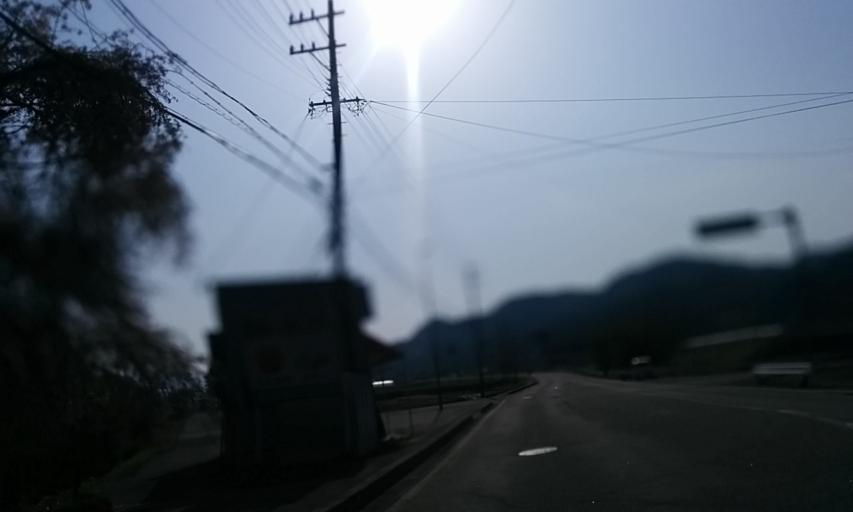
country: JP
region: Gifu
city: Takayama
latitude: 36.1692
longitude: 137.3253
